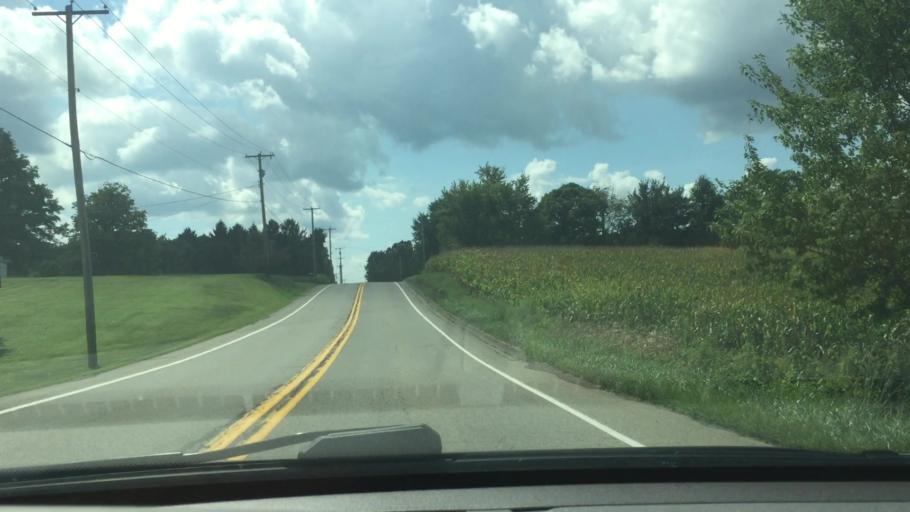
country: US
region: Pennsylvania
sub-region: Lawrence County
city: New Wilmington
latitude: 41.1250
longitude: -80.2343
